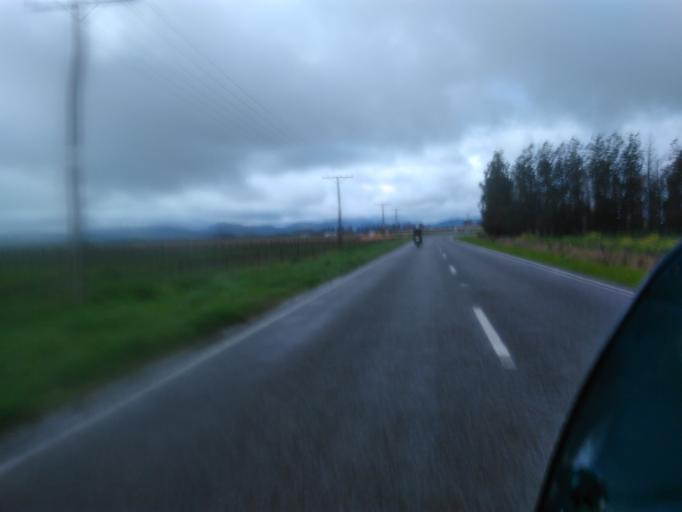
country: NZ
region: Gisborne
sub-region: Gisborne District
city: Gisborne
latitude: -38.6423
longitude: 177.8873
